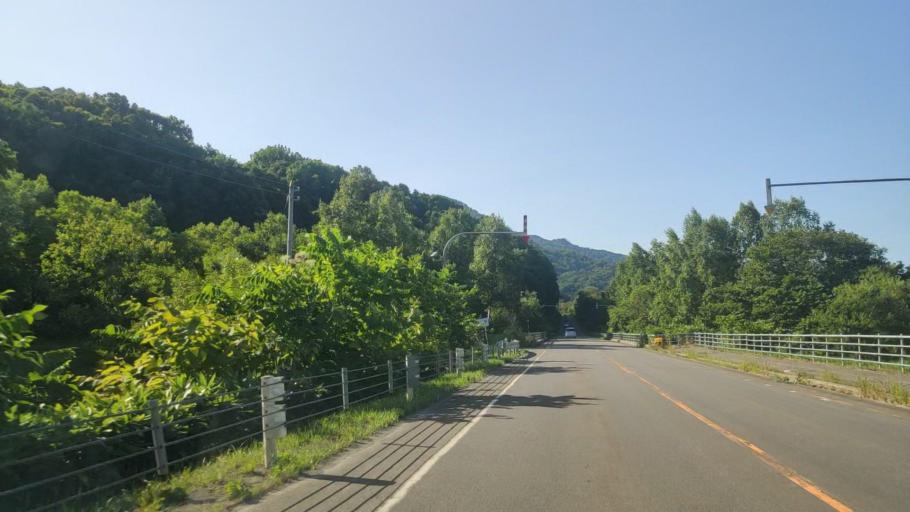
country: JP
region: Hokkaido
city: Nayoro
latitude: 44.7337
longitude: 142.1917
